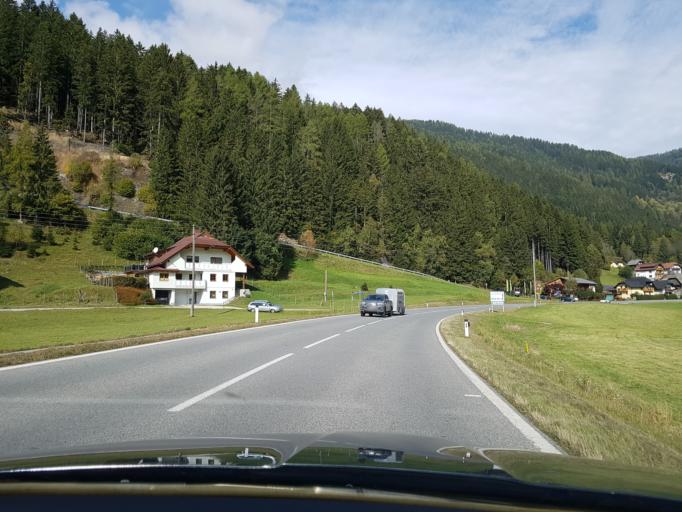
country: AT
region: Carinthia
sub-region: Politischer Bezirk Spittal an der Drau
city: Kleinkirchheim
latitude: 46.8261
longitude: 13.8596
